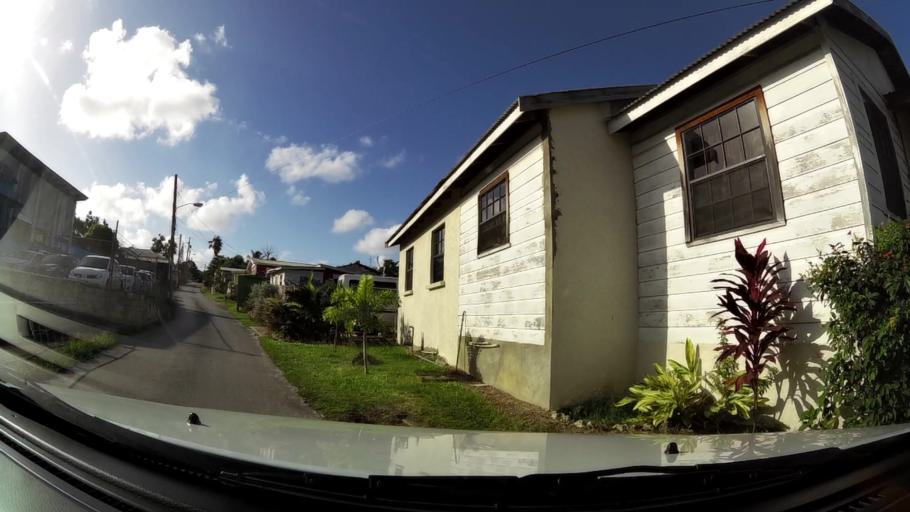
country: BB
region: Saint Michael
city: Bridgetown
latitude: 13.1050
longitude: -59.5980
